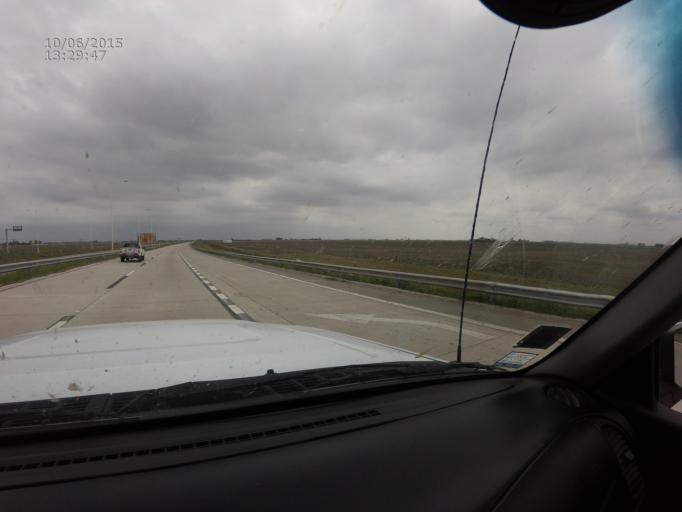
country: AR
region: Cordoba
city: Leones
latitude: -32.6371
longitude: -62.2512
